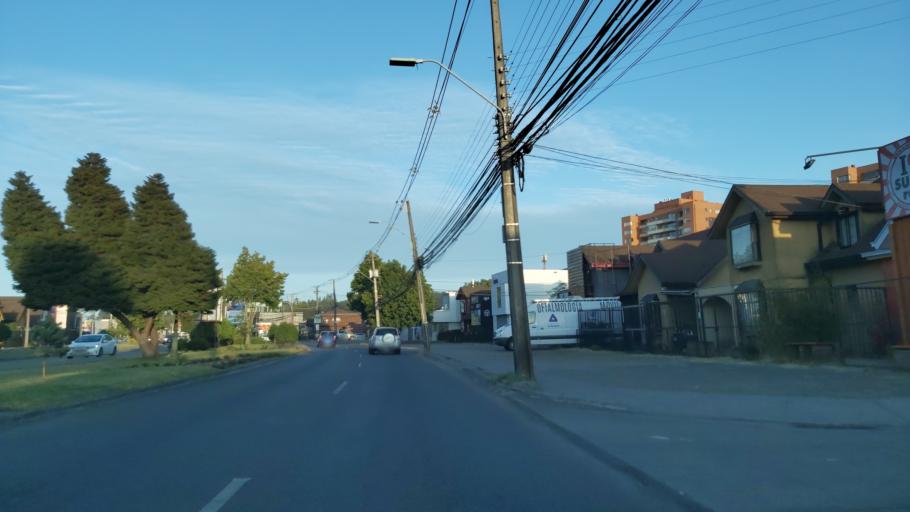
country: CL
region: Biobio
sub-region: Provincia de Concepcion
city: Concepcion
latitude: -36.8443
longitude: -73.0968
